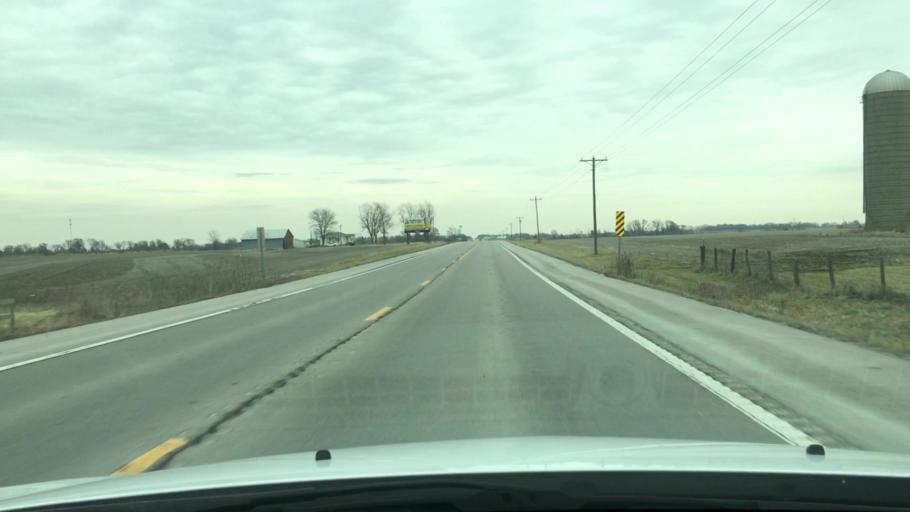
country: US
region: Missouri
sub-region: Montgomery County
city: Wellsville
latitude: 39.1634
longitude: -91.6709
